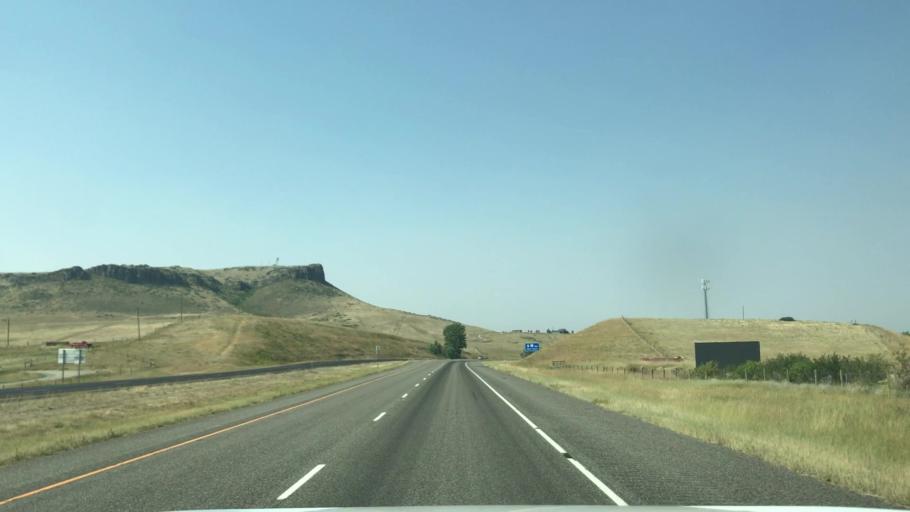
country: US
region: Montana
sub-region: Cascade County
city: Sun Prairie
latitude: 47.2698
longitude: -111.7080
